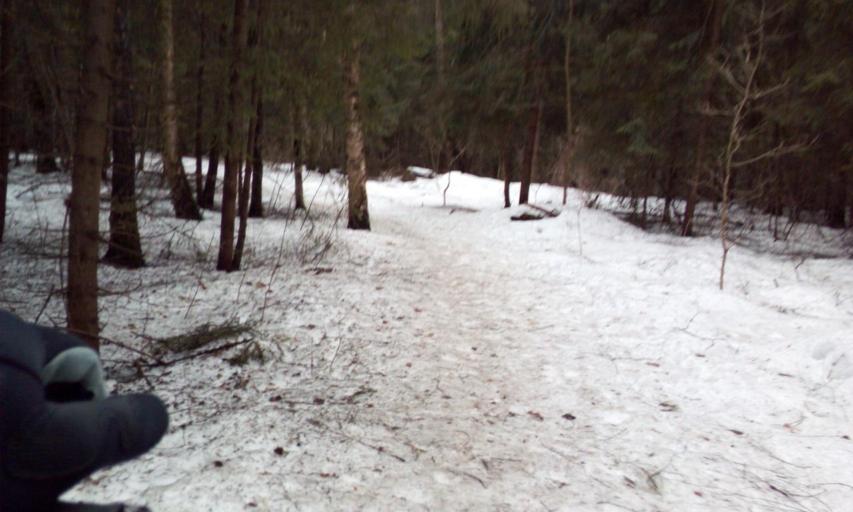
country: RU
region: Moscow
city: Tolstopal'tsevo
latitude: 55.6207
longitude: 37.2522
